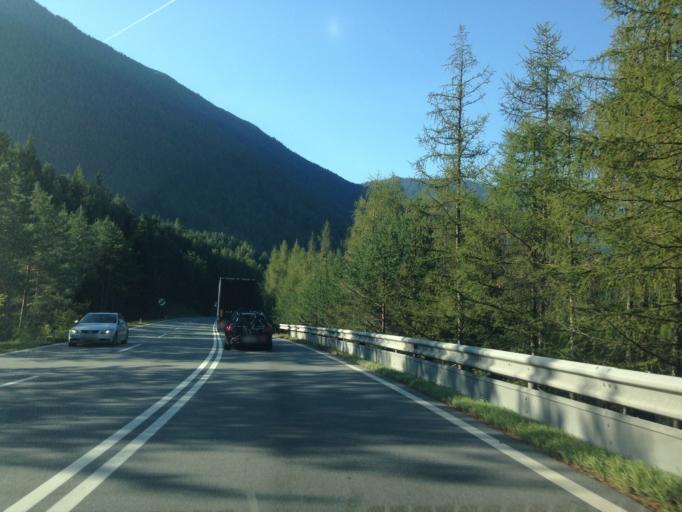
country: AT
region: Tyrol
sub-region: Politischer Bezirk Imst
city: Nassereith
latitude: 47.3075
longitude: 10.8595
